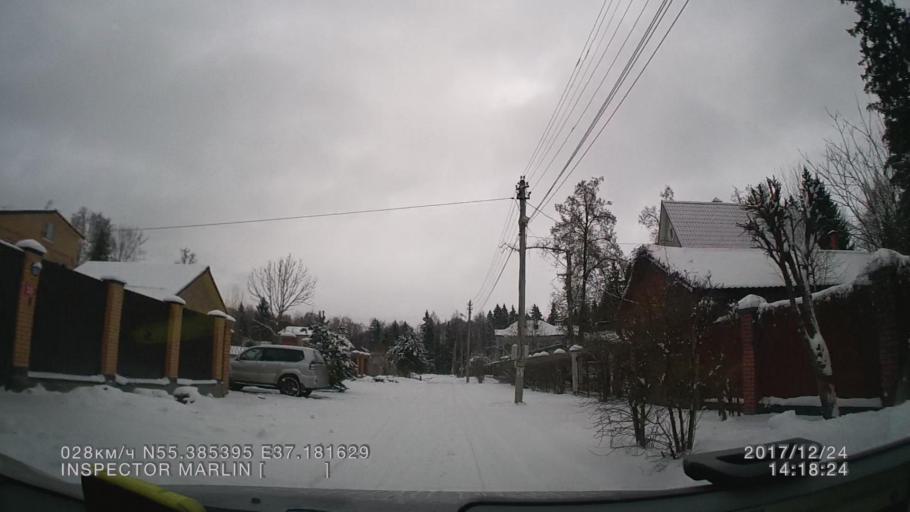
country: RU
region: Moskovskaya
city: Troitsk
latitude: 55.3854
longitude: 37.1817
